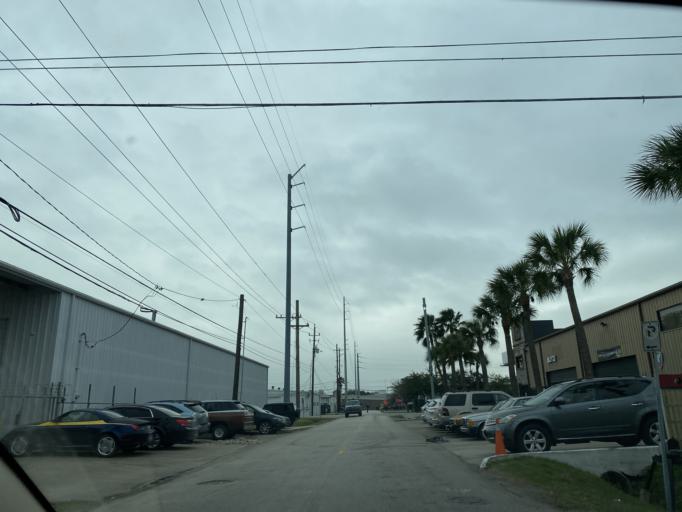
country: US
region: Texas
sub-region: Harris County
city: Bellaire
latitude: 29.7283
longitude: -95.4803
